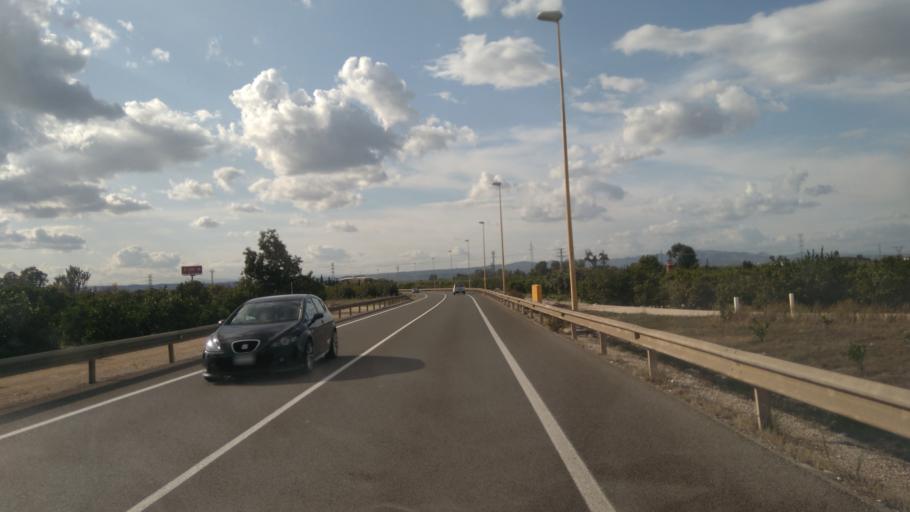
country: ES
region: Valencia
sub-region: Provincia de Valencia
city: Alzira
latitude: 39.1636
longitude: -0.4399
